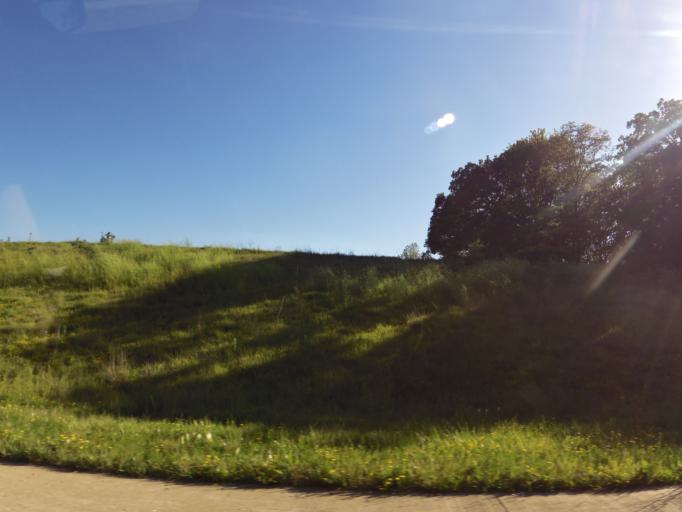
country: US
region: Missouri
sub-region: Pike County
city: Bowling Green
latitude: 39.3654
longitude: -91.2101
